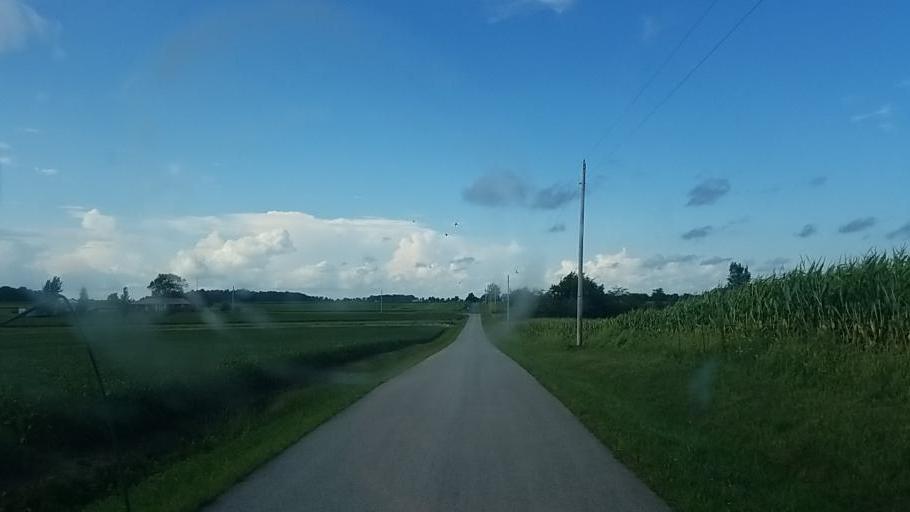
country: US
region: Ohio
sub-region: Hardin County
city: Forest
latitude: 40.7716
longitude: -83.4487
